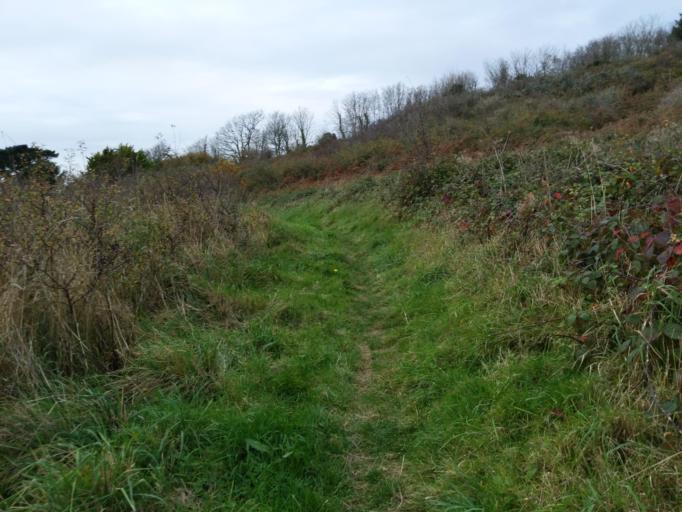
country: GB
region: England
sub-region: Cornwall
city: Looe
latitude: 50.3633
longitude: -4.4266
